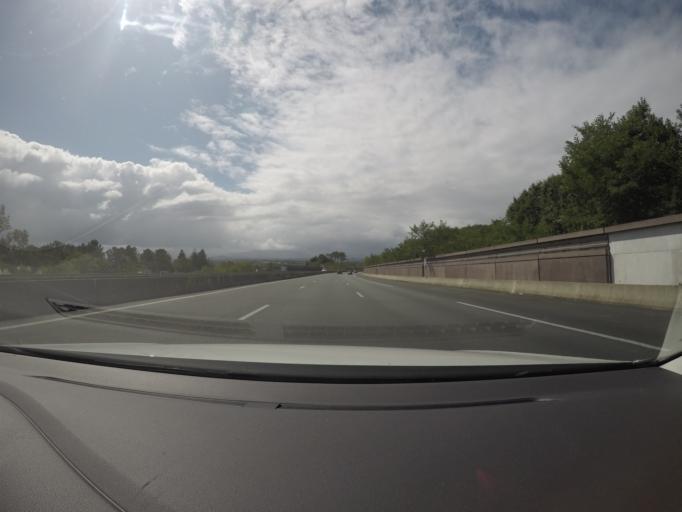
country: FR
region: Aquitaine
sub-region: Departement des Pyrenees-Atlantiques
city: Bassussarry
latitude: 43.4501
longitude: -1.5347
